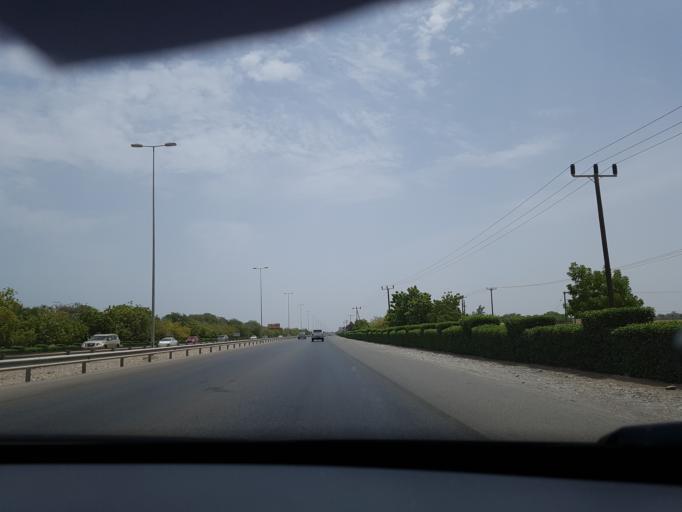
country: OM
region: Muhafazat Masqat
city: As Sib al Jadidah
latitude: 23.6906
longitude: 58.0416
